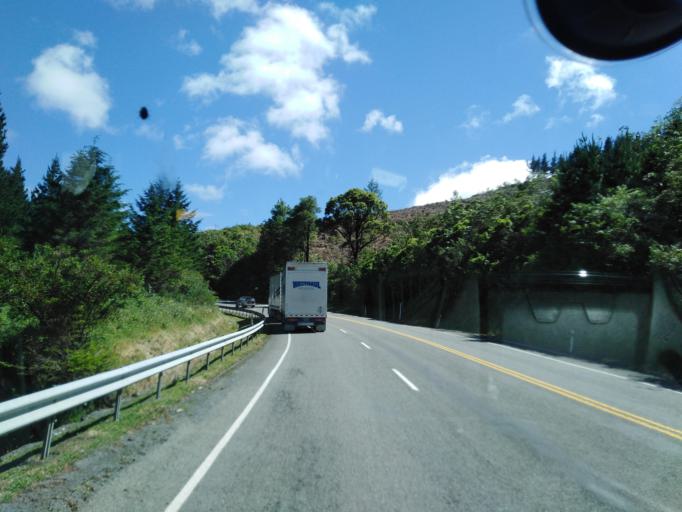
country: NZ
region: Nelson
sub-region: Nelson City
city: Nelson
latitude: -41.1929
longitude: 173.5574
